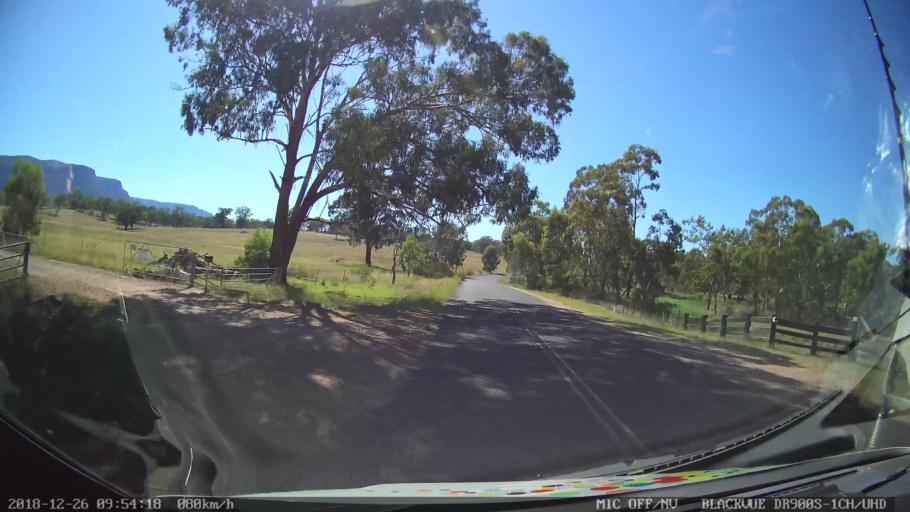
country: AU
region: New South Wales
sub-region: Mid-Western Regional
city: Kandos
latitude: -33.0290
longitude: 150.1600
